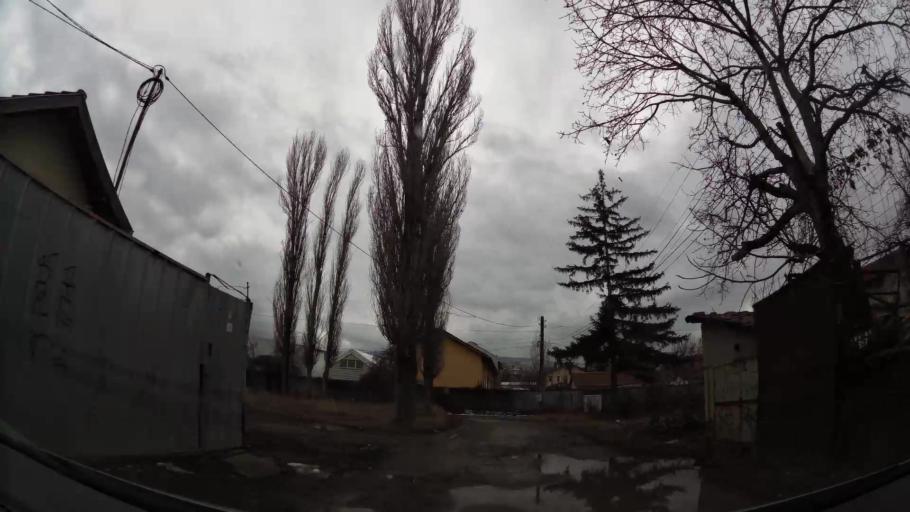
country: BG
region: Sofia-Capital
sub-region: Stolichna Obshtina
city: Sofia
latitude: 42.7212
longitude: 23.2781
